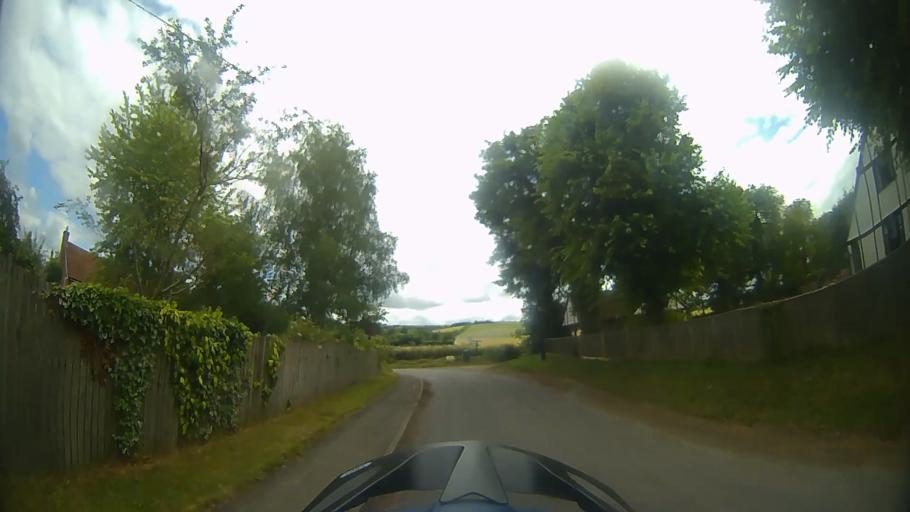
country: GB
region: England
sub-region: Oxfordshire
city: Wantage
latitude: 51.5733
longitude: -1.4515
